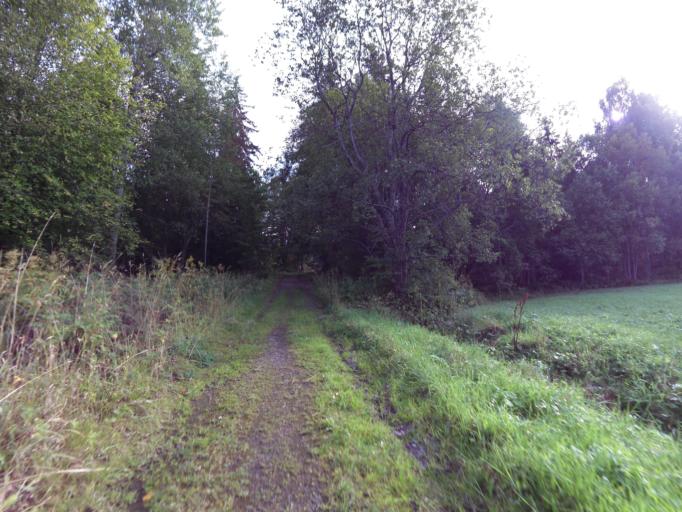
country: SE
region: Gaevleborg
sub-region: Gavle Kommun
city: Gavle
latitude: 60.6790
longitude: 17.2306
